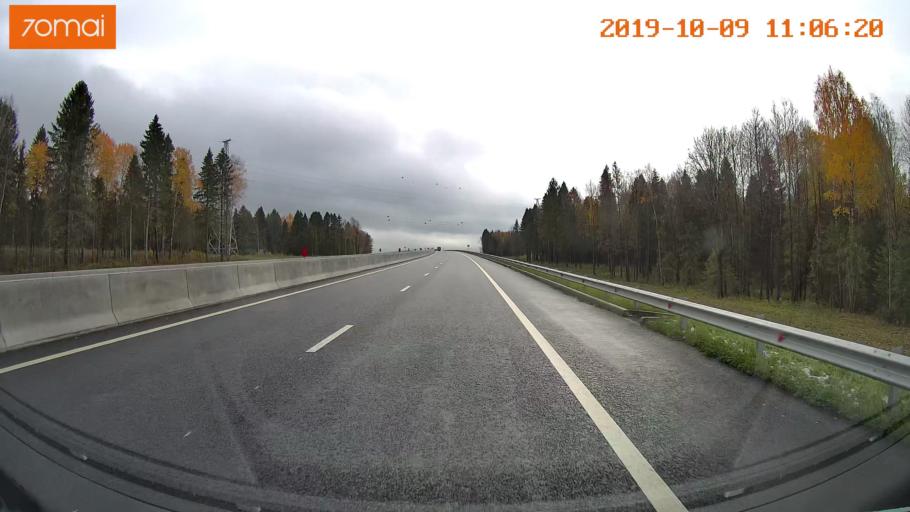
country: RU
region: Vologda
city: Vologda
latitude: 59.1879
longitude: 39.7598
